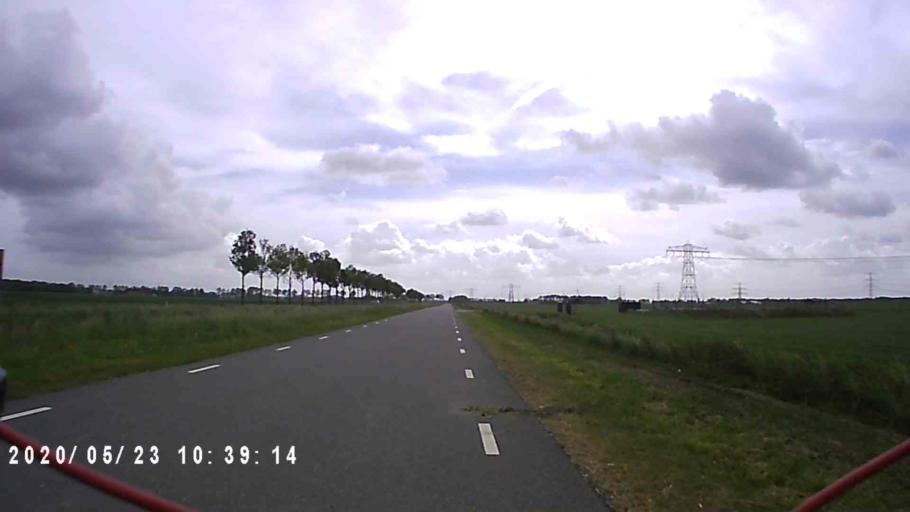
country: NL
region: Groningen
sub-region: Gemeente Appingedam
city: Appingedam
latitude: 53.3026
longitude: 6.8817
